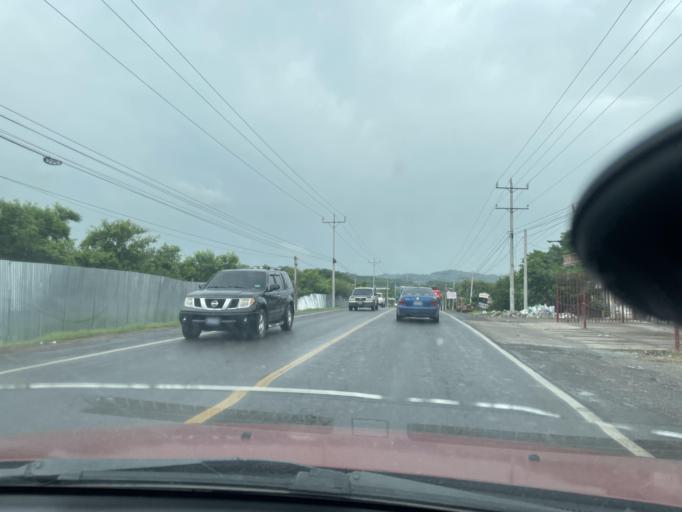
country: SV
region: San Miguel
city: San Miguel
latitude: 13.5033
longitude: -88.1593
